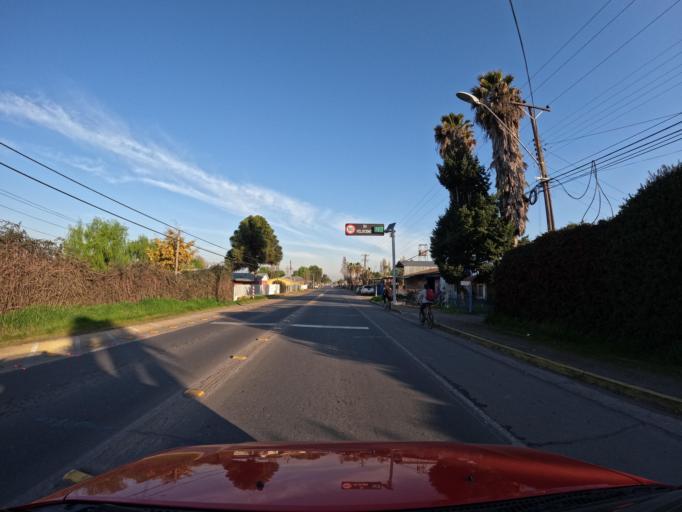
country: CL
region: Maule
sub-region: Provincia de Curico
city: Curico
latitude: -34.9431
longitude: -71.2613
